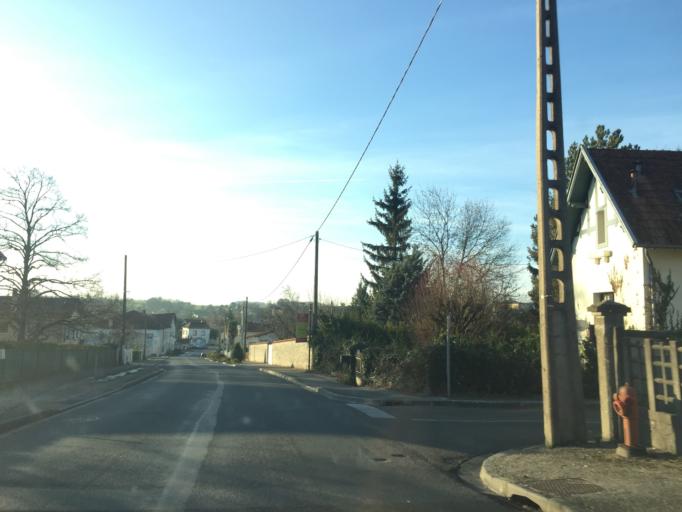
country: FR
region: Poitou-Charentes
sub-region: Departement de la Charente
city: Chalais
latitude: 45.2711
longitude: 0.0479
